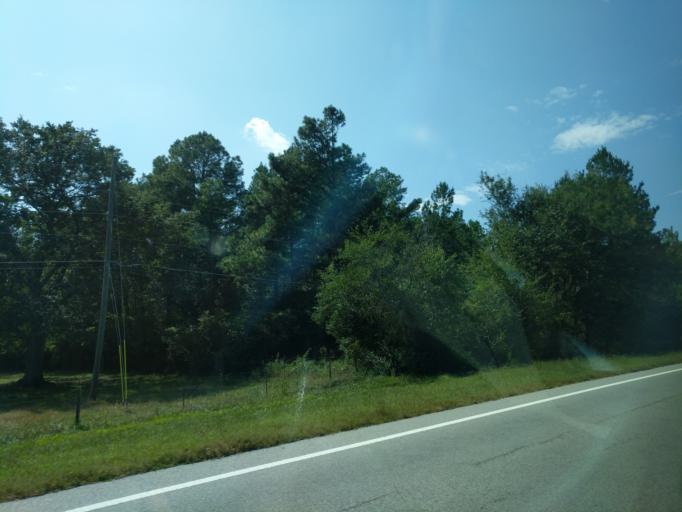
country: US
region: Georgia
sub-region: Franklin County
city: Gumlog
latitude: 34.4560
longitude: -83.0504
